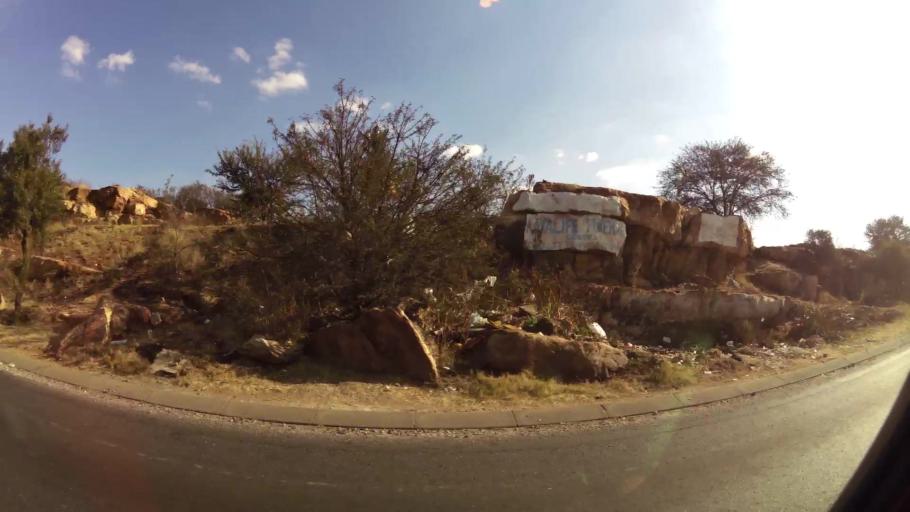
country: ZA
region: Gauteng
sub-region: City of Johannesburg Metropolitan Municipality
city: Soweto
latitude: -26.2300
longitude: 27.8734
